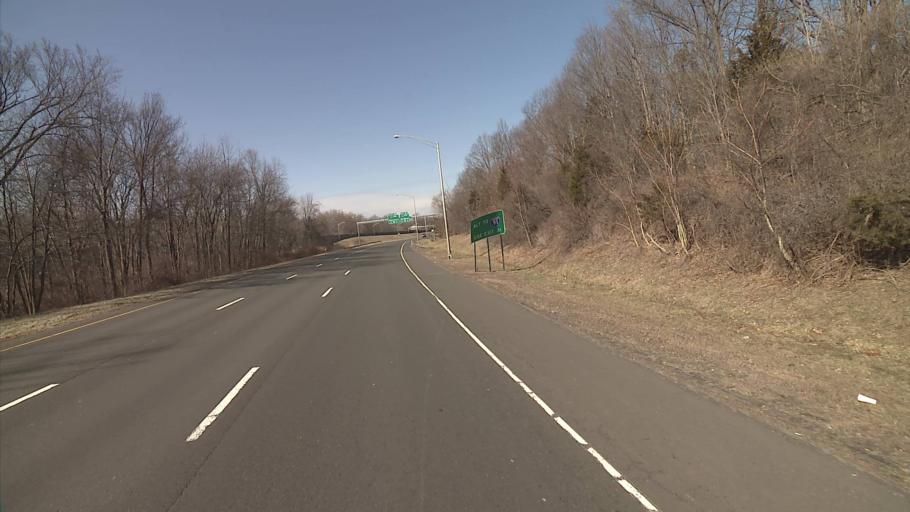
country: US
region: Connecticut
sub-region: Hartford County
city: Newington
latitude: 41.7168
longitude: -72.7694
